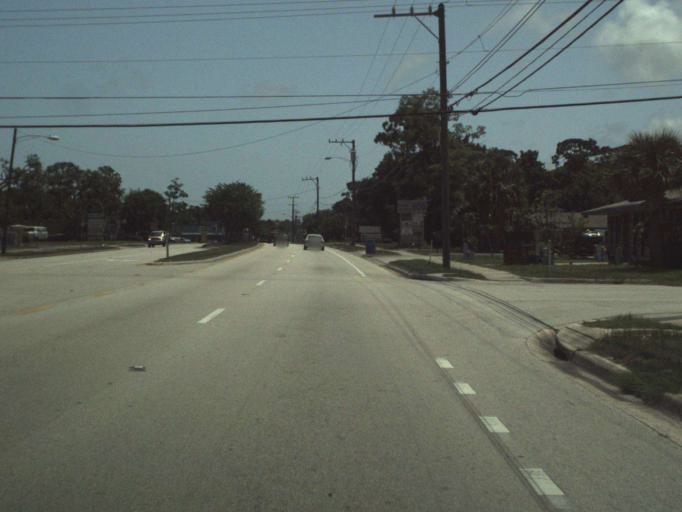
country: US
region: Florida
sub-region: Volusia County
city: Ormond Beach
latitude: 29.2687
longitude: -81.0547
